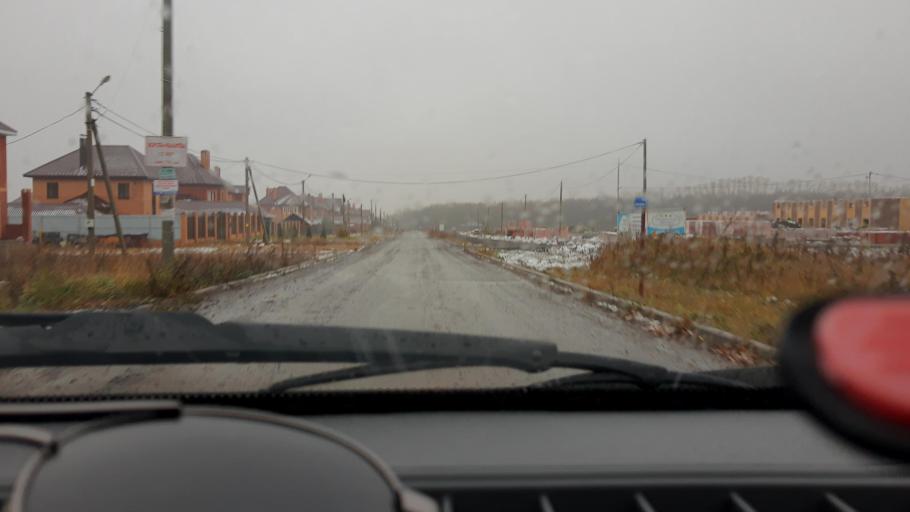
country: RU
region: Bashkortostan
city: Kabakovo
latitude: 54.6157
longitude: 56.1406
